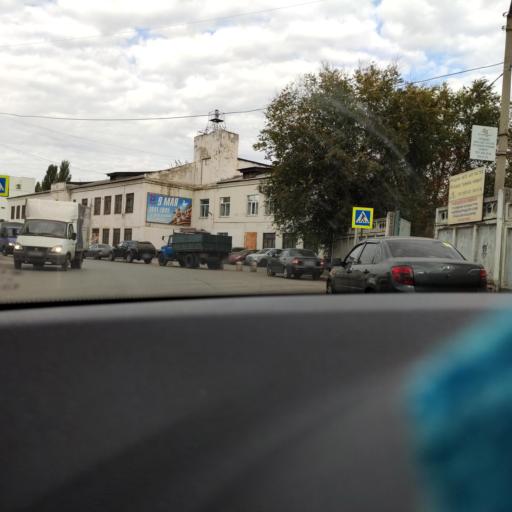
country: RU
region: Samara
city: Samara
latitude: 53.1998
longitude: 50.2557
